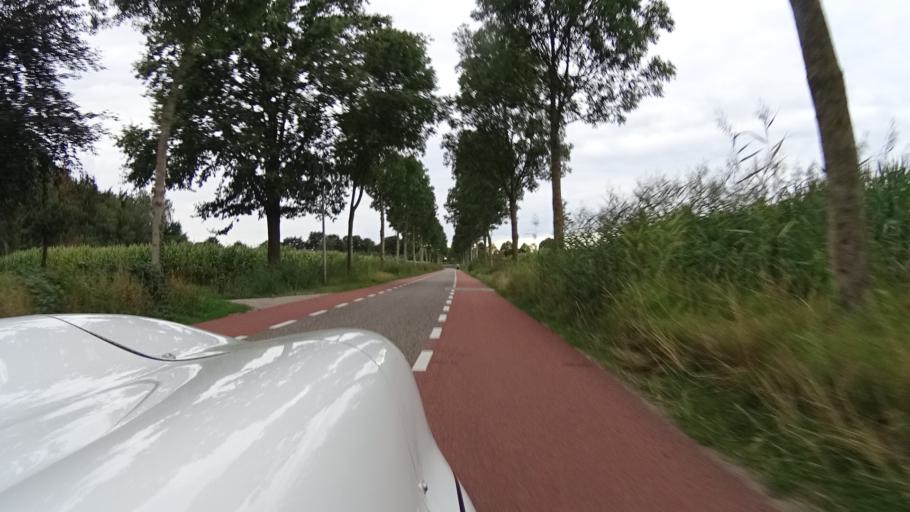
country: NL
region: North Brabant
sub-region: Gemeente Veghel
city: Mariaheide
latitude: 51.6504
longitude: 5.5776
